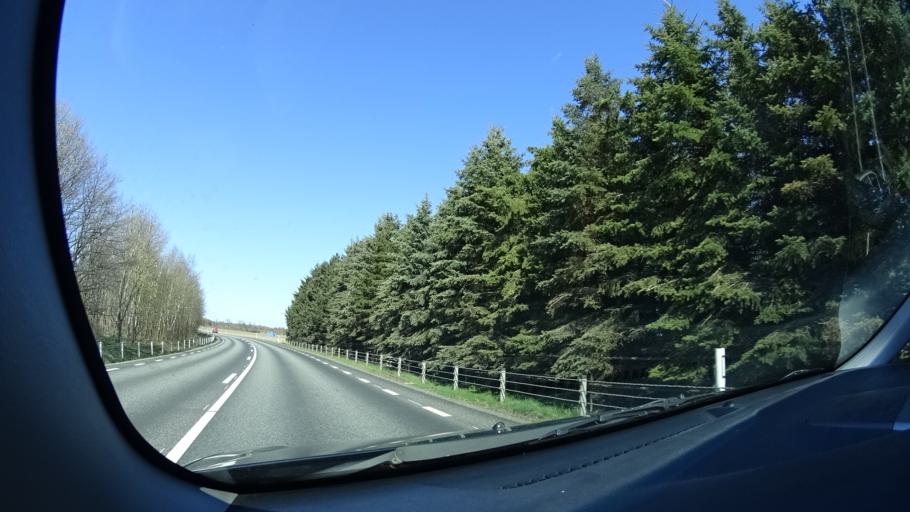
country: SE
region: Skane
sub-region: Angelholms Kommun
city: AEngelholm
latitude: 56.1952
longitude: 12.8477
